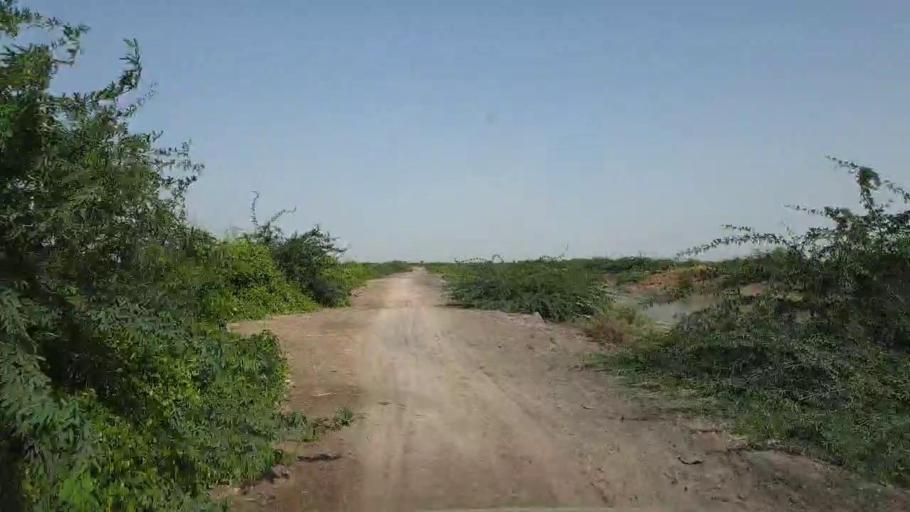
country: PK
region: Sindh
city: Tando Bago
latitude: 24.7105
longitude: 69.0716
